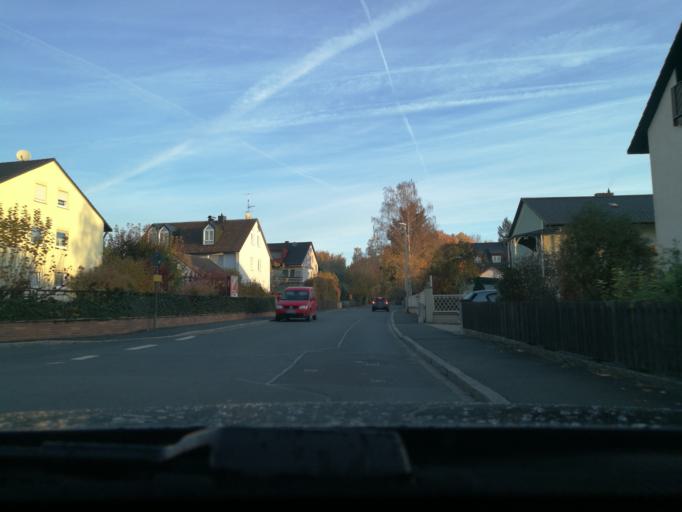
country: DE
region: Bavaria
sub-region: Regierungsbezirk Mittelfranken
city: Herzogenaurach
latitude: 49.5649
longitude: 10.9153
